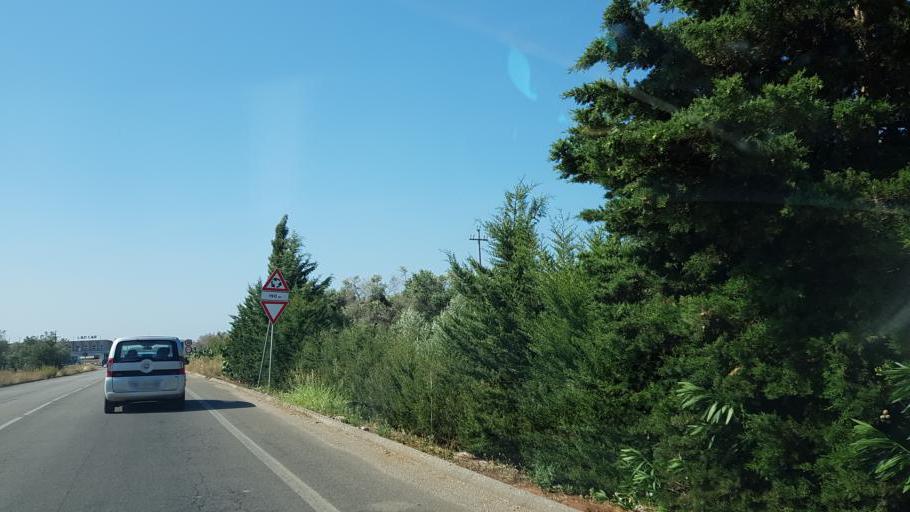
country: IT
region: Apulia
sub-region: Provincia di Lecce
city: Veglie
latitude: 40.3322
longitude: 17.9427
